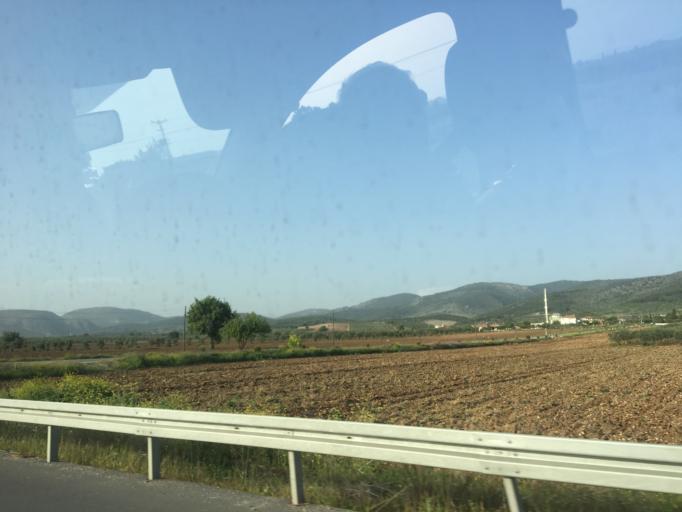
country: TR
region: Manisa
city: Golmarmara
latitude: 38.7910
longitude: 27.9009
